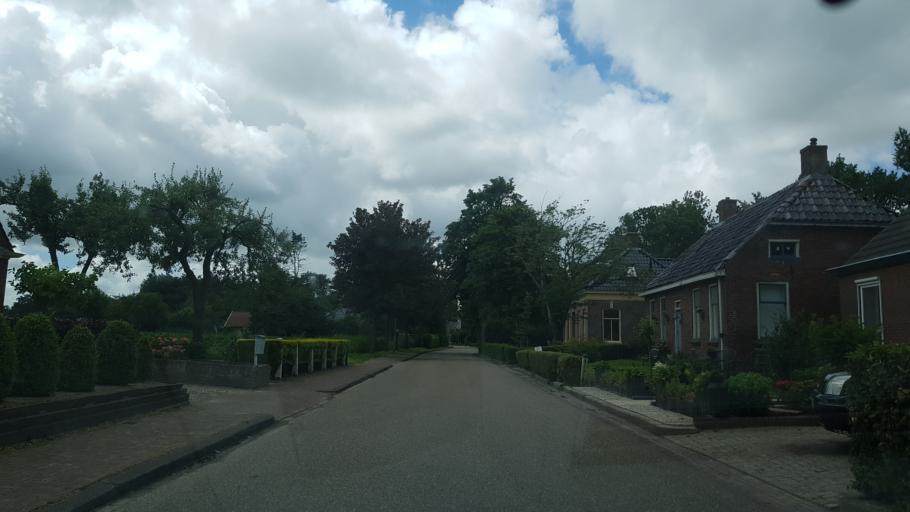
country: NL
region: Groningen
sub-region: Gemeente Winsum
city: Winsum
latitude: 53.3999
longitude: 6.4877
